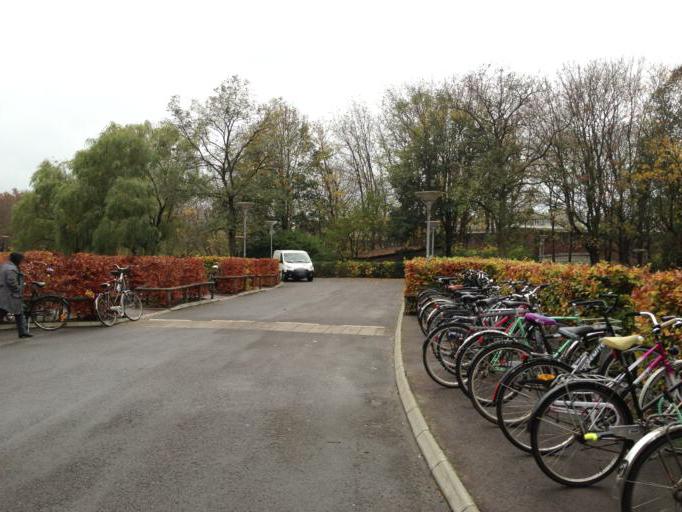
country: SE
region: Skane
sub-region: Lunds Kommun
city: Lund
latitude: 55.7094
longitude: 13.2094
